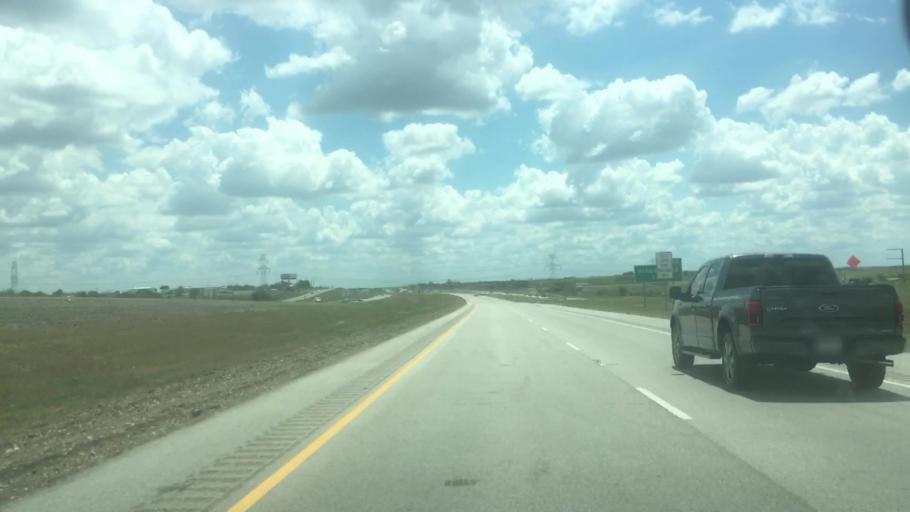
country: US
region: Texas
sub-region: Caldwell County
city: Uhland
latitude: 30.0023
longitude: -97.6870
